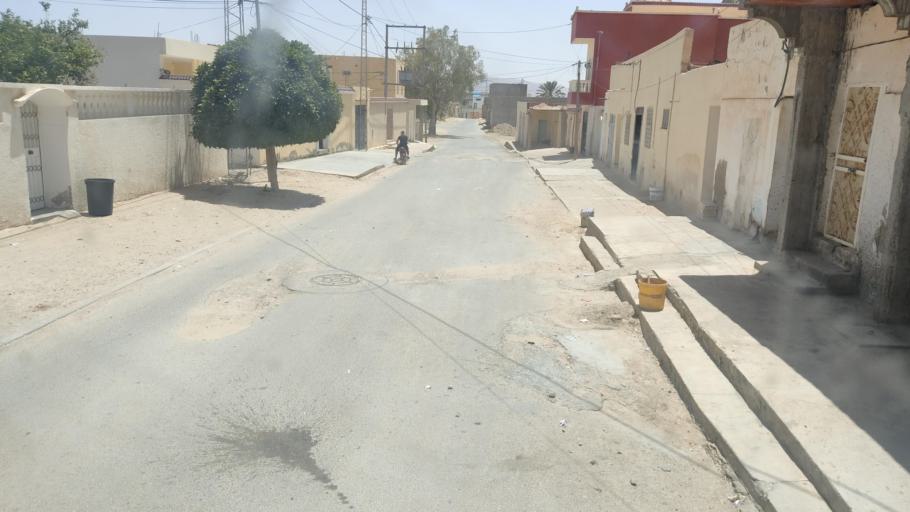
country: TN
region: Gafsa
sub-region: Gafsa Municipality
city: Gafsa
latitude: 34.3382
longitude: 8.9422
